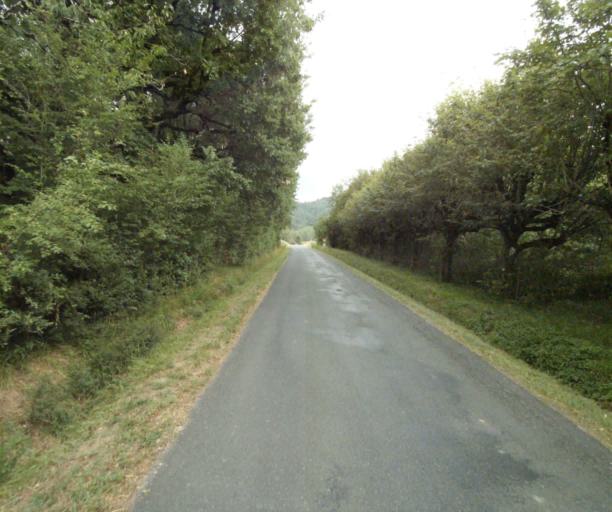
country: FR
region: Midi-Pyrenees
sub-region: Departement du Tarn
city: Soreze
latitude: 43.4654
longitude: 2.0839
